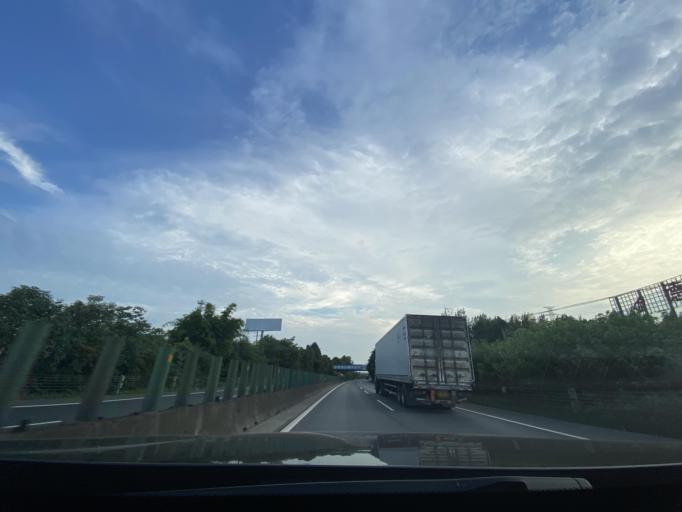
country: CN
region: Sichuan
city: Luojiang
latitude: 31.3711
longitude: 104.5435
